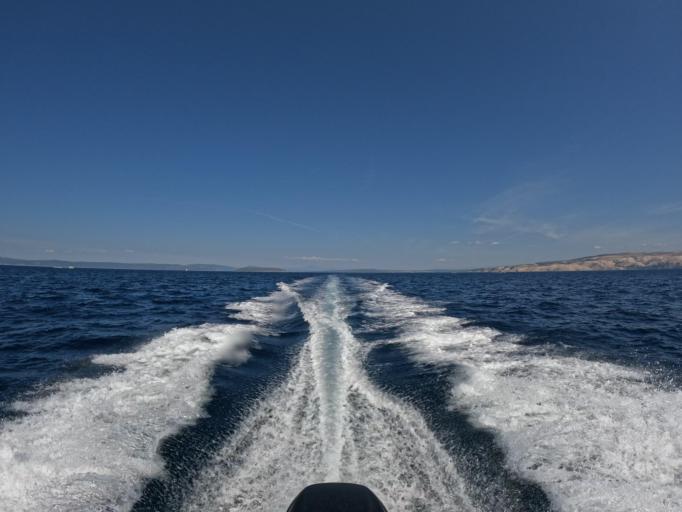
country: HR
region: Primorsko-Goranska
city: Punat
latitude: 44.9008
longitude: 14.6315
